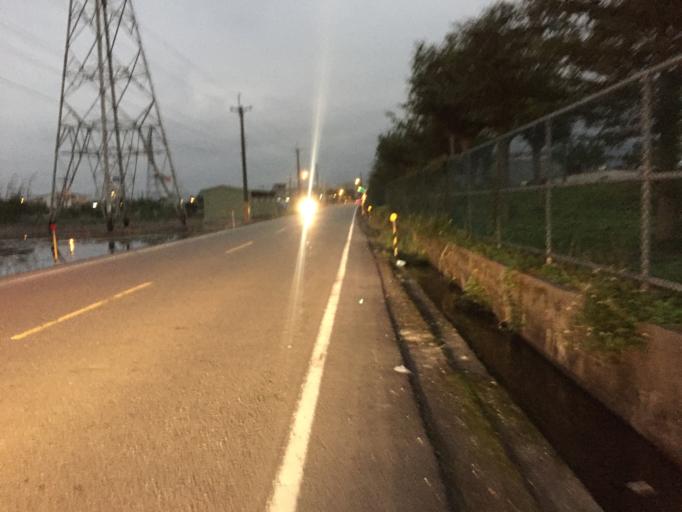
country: TW
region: Taiwan
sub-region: Yilan
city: Yilan
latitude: 24.6596
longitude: 121.7789
